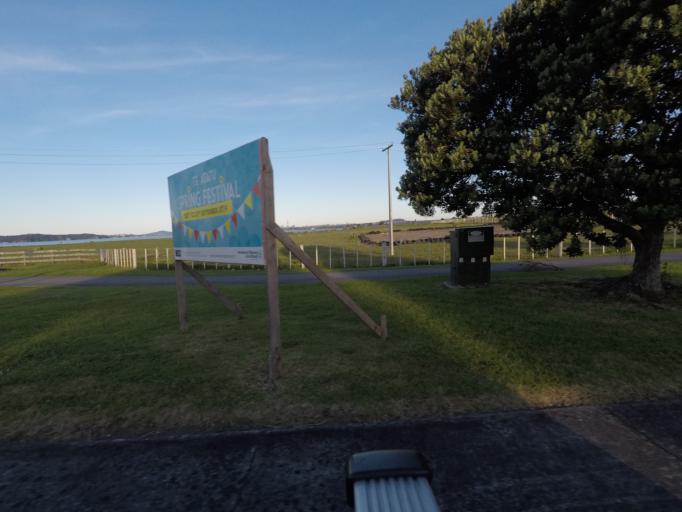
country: NZ
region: Auckland
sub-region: Auckland
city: Rosebank
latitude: -36.8529
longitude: 174.6510
